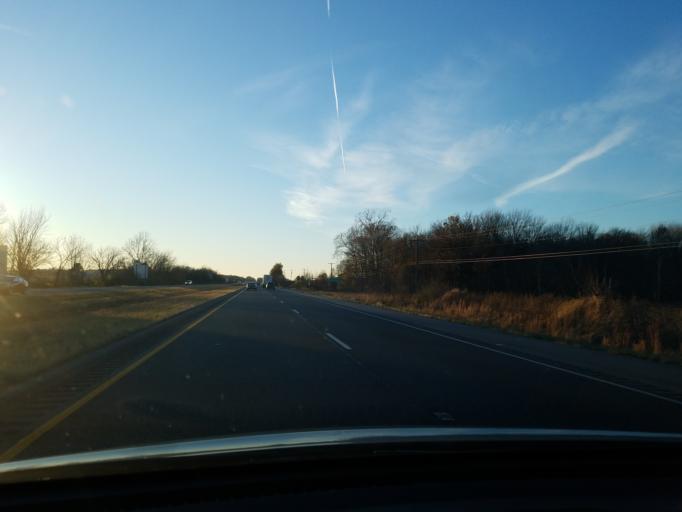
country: US
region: Indiana
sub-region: Gibson County
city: Haubstadt
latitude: 38.1671
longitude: -87.5767
